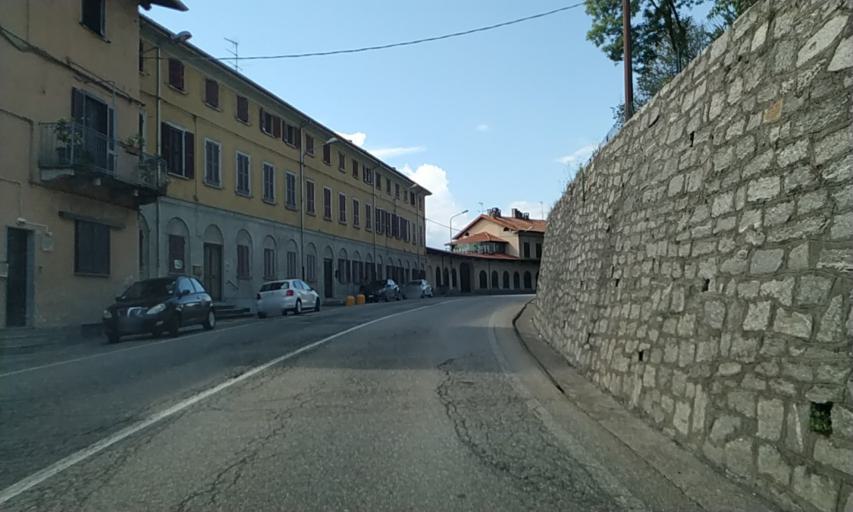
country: IT
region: Piedmont
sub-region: Provincia di Novara
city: Romagnano Sesia
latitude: 45.6354
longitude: 8.3795
